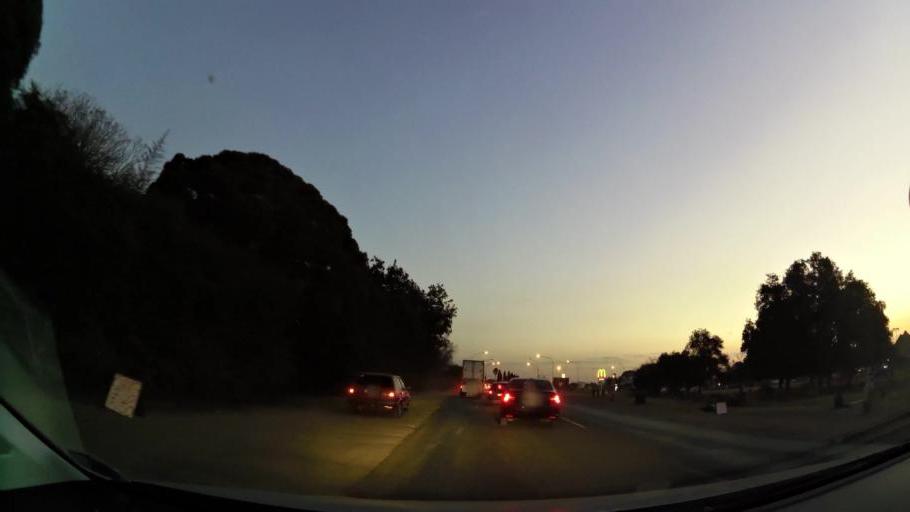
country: ZA
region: Gauteng
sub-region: City of Johannesburg Metropolitan Municipality
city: Modderfontein
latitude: -26.0643
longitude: 28.2221
